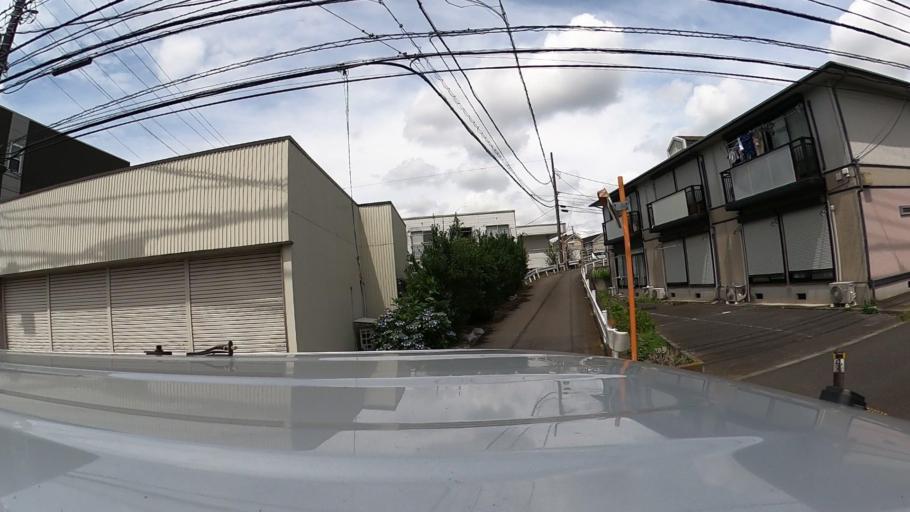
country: JP
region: Kanagawa
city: Fujisawa
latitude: 35.4052
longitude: 139.4697
